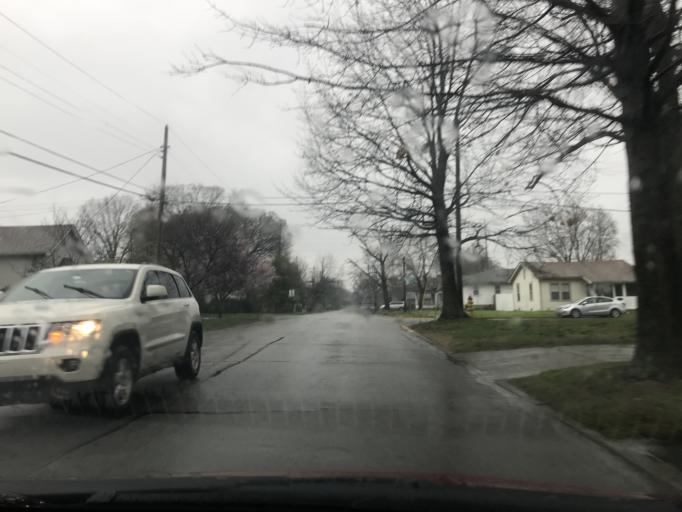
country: US
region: Indiana
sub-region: Clark County
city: Clarksville
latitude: 38.2775
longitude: -85.7601
